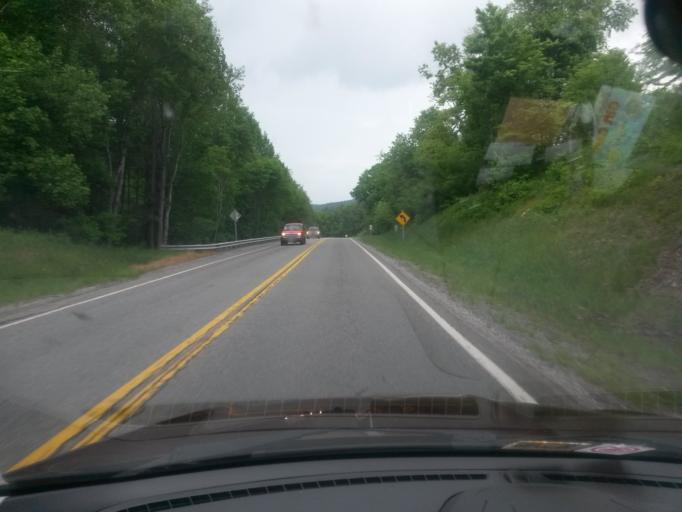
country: US
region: Virginia
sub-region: Floyd County
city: Floyd
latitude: 36.9469
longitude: -80.3594
